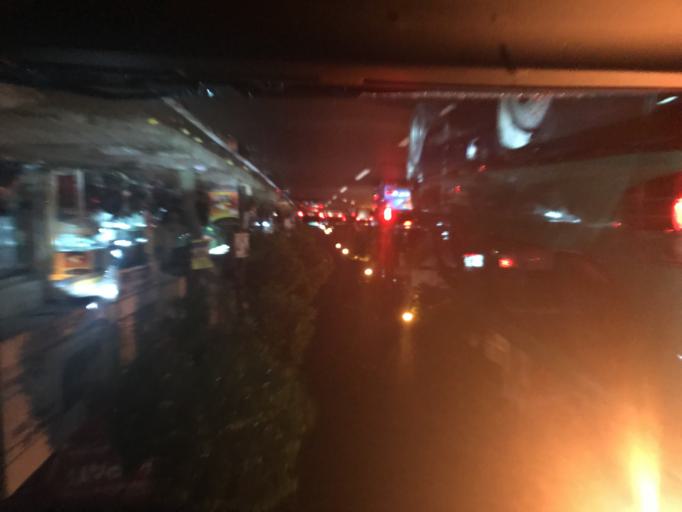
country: ID
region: West Java
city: Bandung
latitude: -6.9101
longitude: 107.6407
